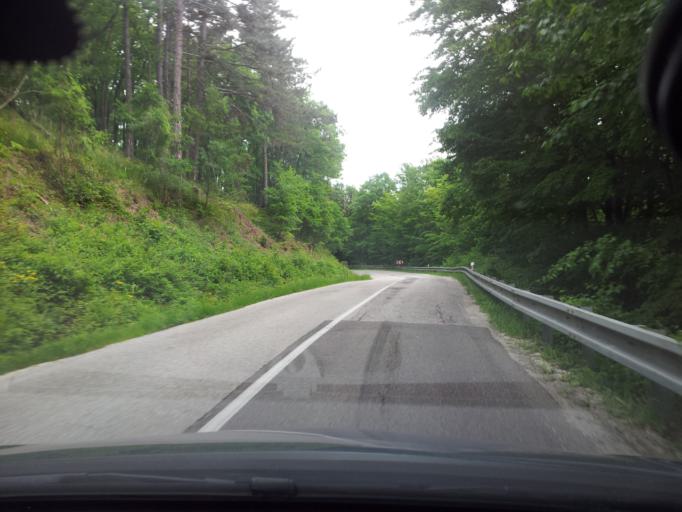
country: SK
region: Nitriansky
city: Partizanske
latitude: 48.5719
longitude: 18.4561
